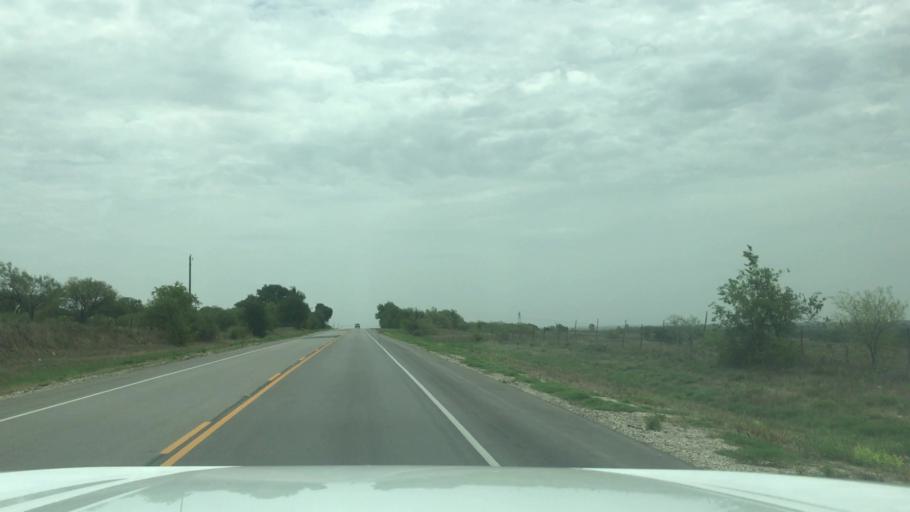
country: US
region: Texas
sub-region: Erath County
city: Dublin
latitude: 32.0808
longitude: -98.2446
